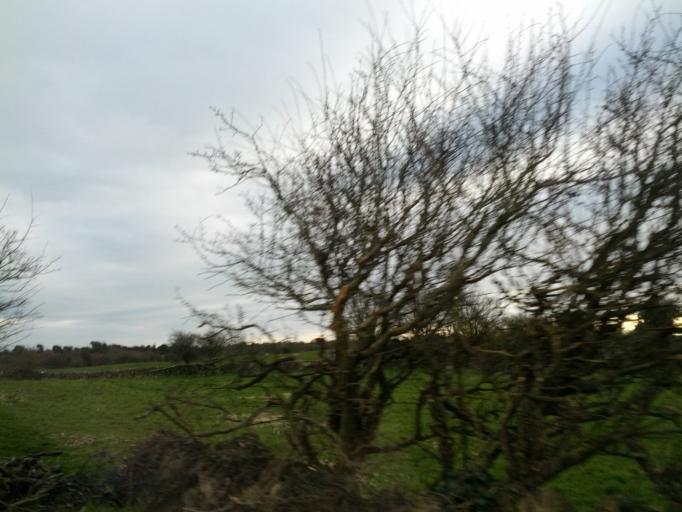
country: IE
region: Connaught
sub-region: County Galway
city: Gort
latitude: 53.1551
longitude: -8.8642
